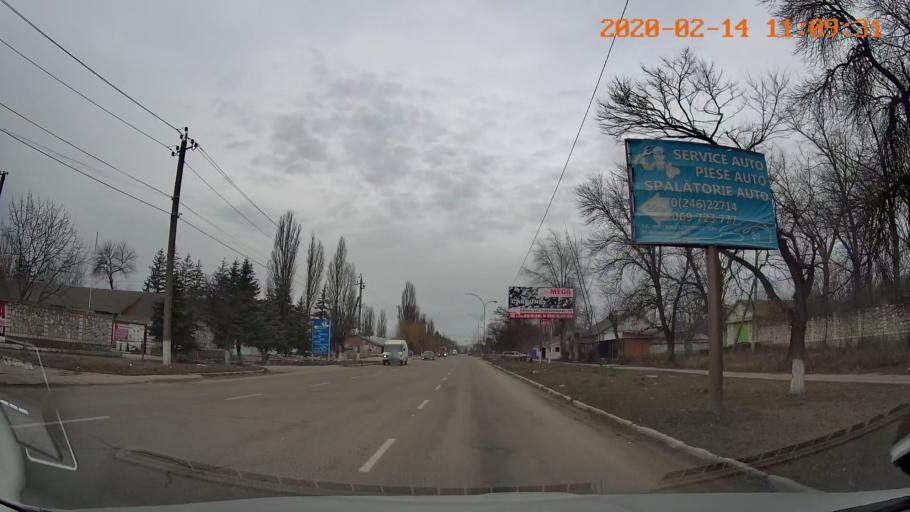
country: MD
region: Raionul Edinet
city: Edinet
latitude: 48.1791
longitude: 27.2933
